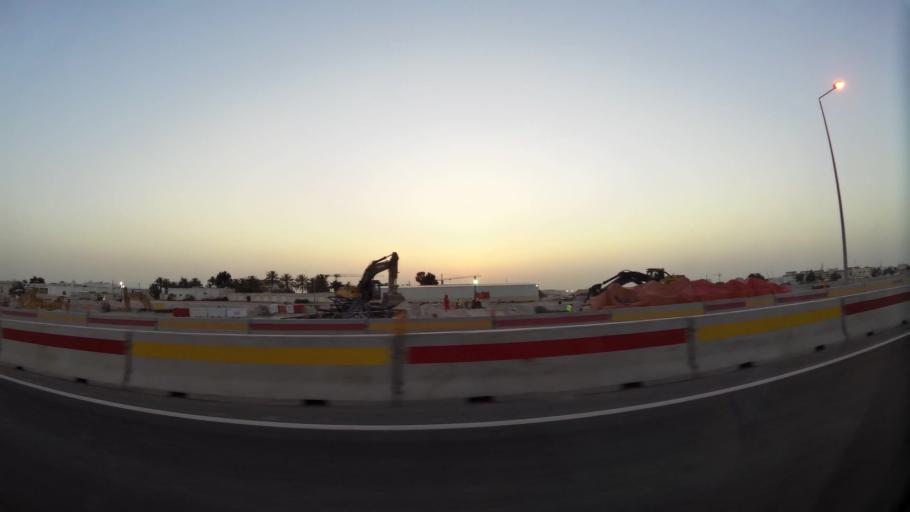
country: QA
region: Baladiyat ar Rayyan
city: Ar Rayyan
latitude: 25.3029
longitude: 51.4652
